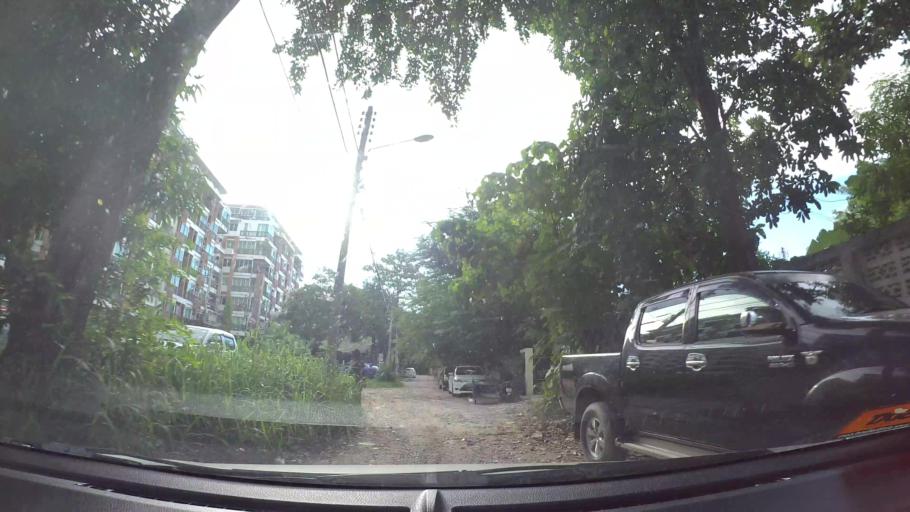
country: TH
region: Chon Buri
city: Phatthaya
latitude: 12.9121
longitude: 100.8732
